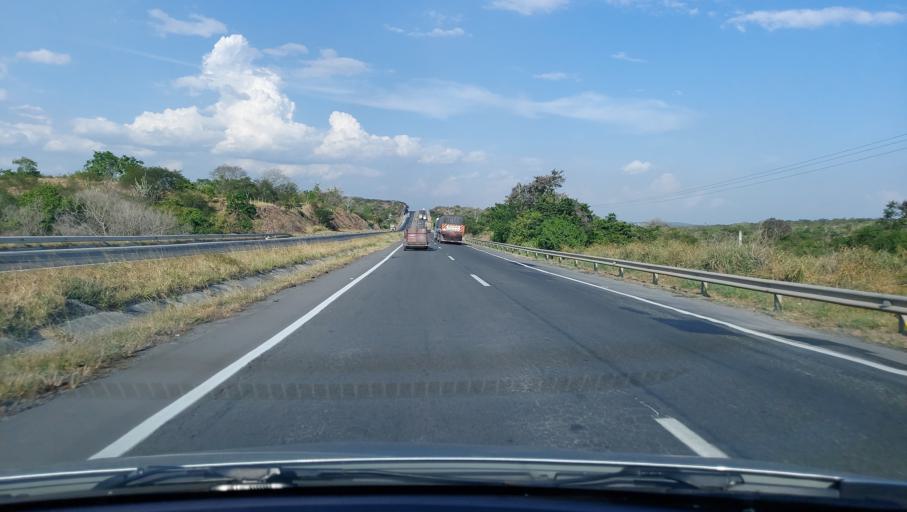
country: BR
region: Bahia
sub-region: Santo Estevao
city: Santo Estevao
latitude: -12.4316
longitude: -39.2157
